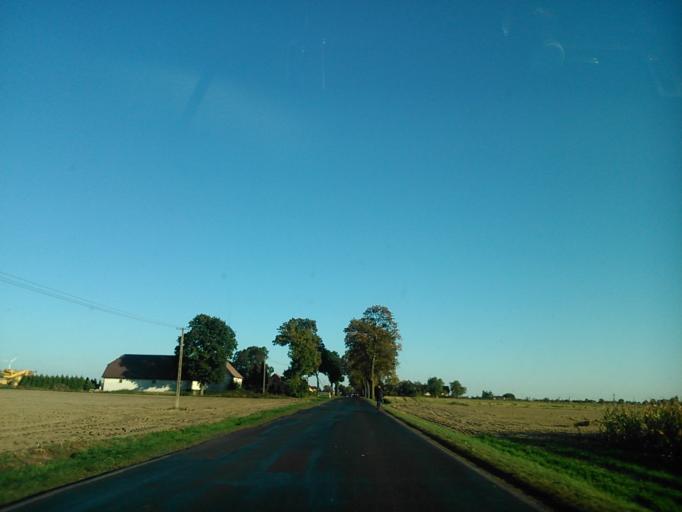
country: PL
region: Kujawsko-Pomorskie
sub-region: Powiat golubsko-dobrzynski
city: Golub-Dobrzyn
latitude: 53.1320
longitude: 19.0169
